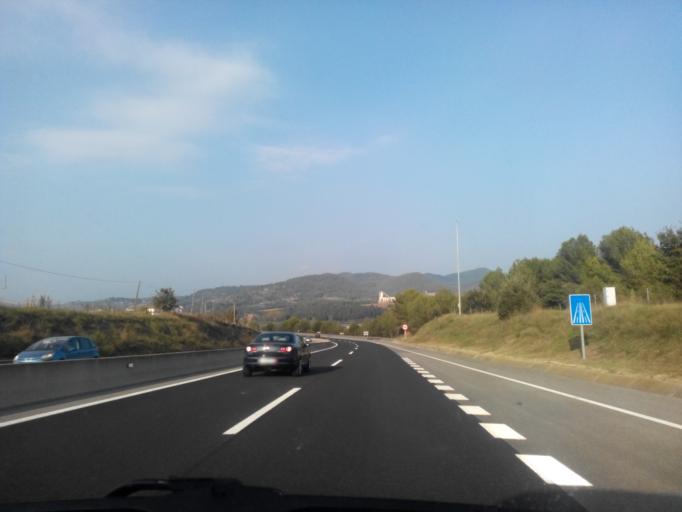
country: ES
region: Catalonia
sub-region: Provincia de Barcelona
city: Sallent
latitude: 41.7929
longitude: 1.8974
